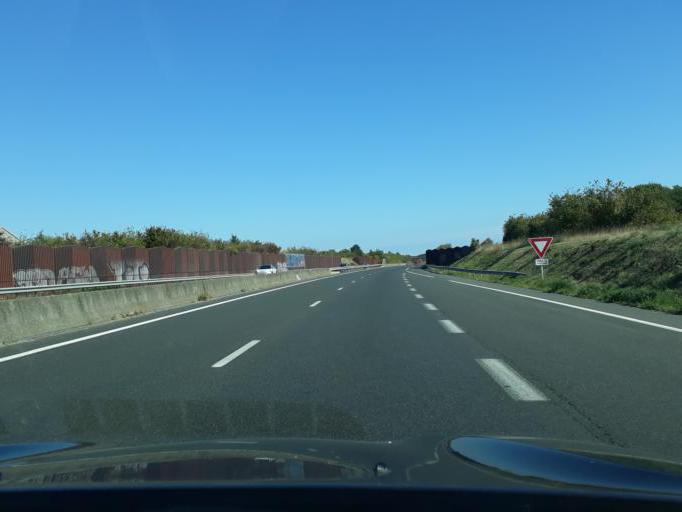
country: FR
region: Centre
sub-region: Departement d'Indre-et-Loire
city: Ballan-Mire
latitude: 47.3344
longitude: 0.6171
